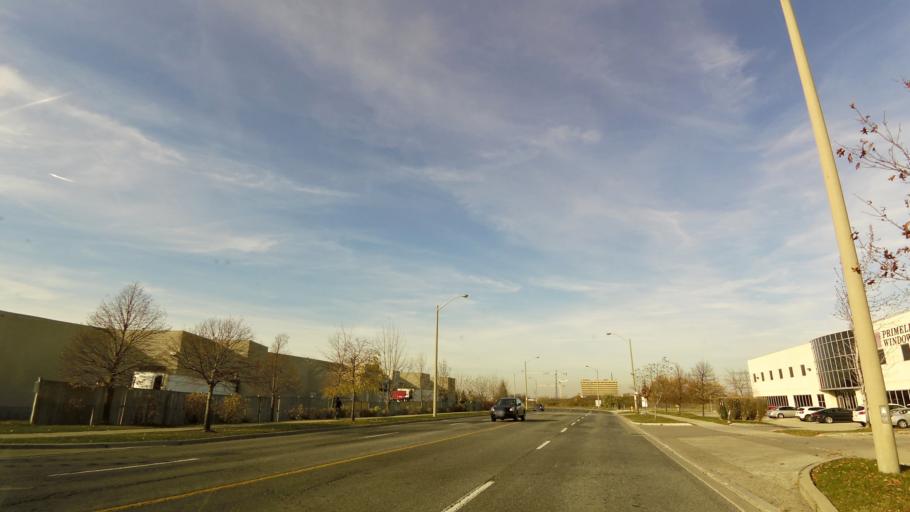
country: CA
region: Ontario
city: Etobicoke
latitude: 43.7209
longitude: -79.5946
